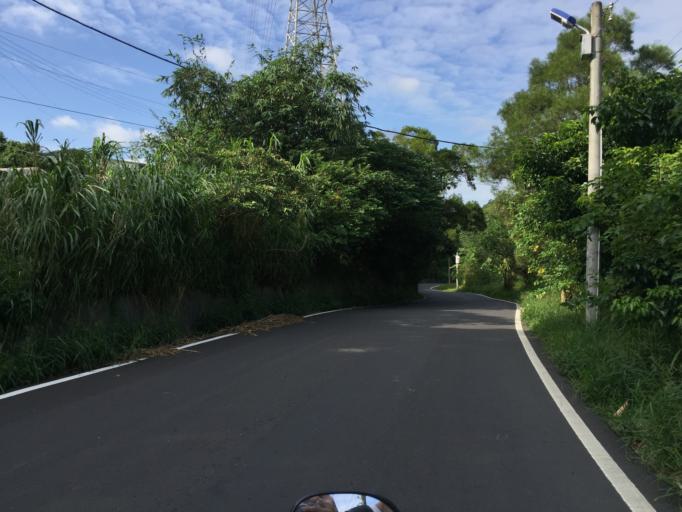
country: TW
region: Taiwan
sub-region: Hsinchu
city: Hsinchu
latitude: 24.7601
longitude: 120.9430
